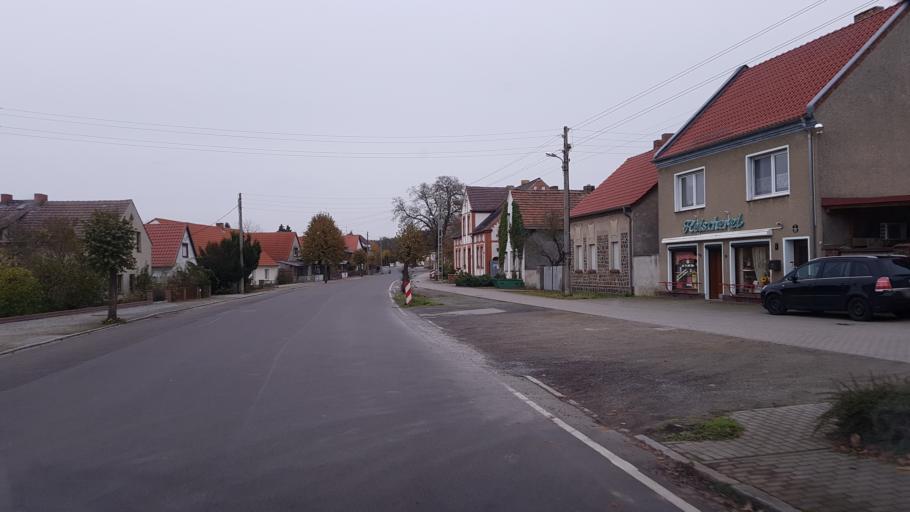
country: DE
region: Brandenburg
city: Crinitz
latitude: 51.7383
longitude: 13.7615
